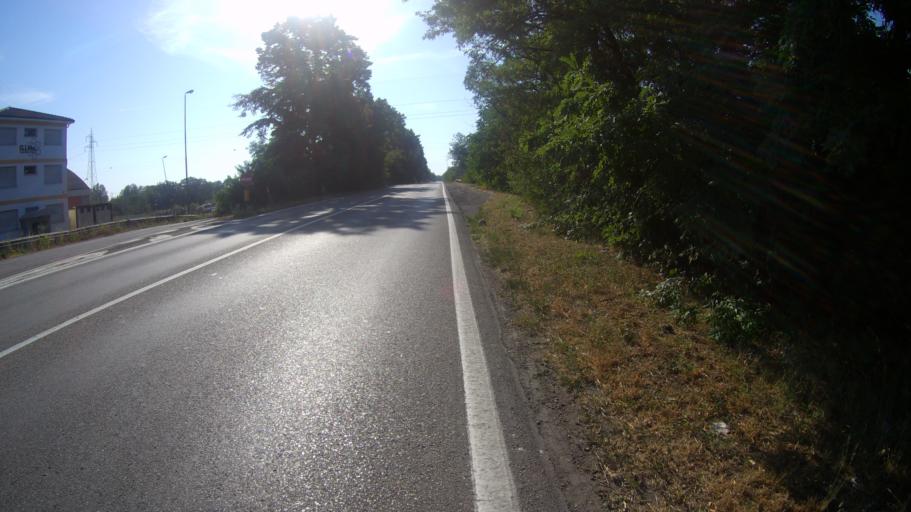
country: IT
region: Emilia-Romagna
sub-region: Provincia di Reggio Emilia
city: Rubiera
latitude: 44.6515
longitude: 10.7906
